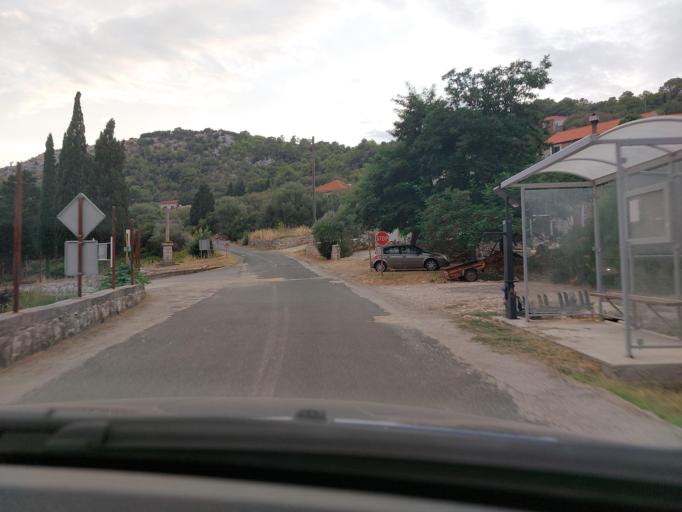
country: HR
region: Dubrovacko-Neretvanska
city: Smokvica
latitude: 42.7659
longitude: 16.8951
